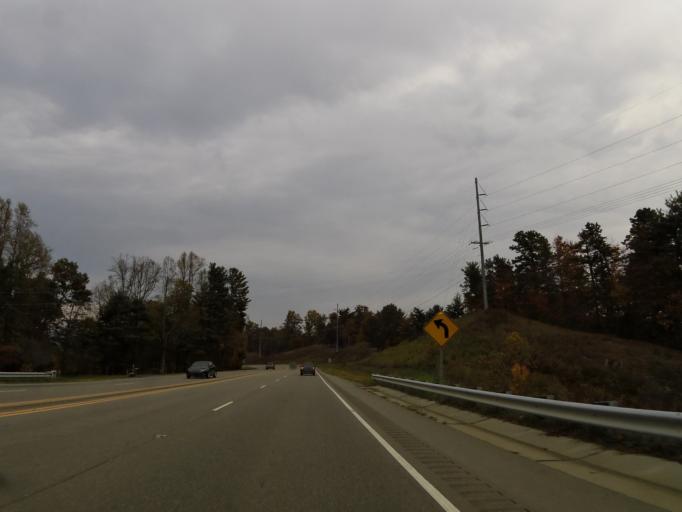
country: US
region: North Carolina
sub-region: Watauga County
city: Blowing Rock
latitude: 36.0660
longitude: -81.6138
